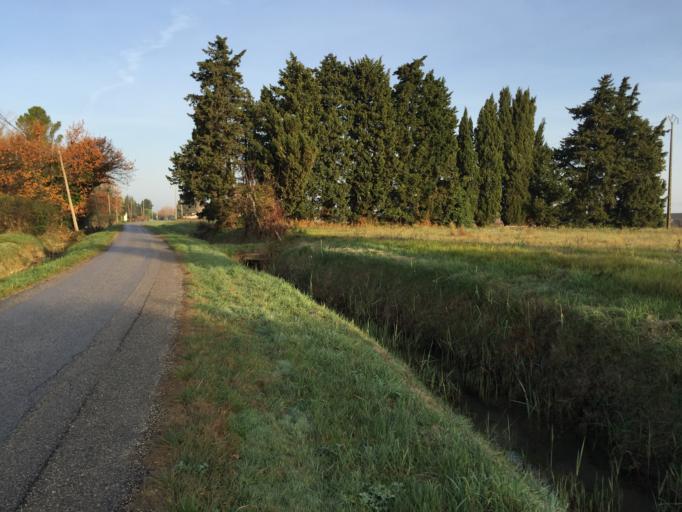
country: FR
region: Provence-Alpes-Cote d'Azur
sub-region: Departement du Vaucluse
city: Caderousse
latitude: 44.1207
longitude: 4.7697
